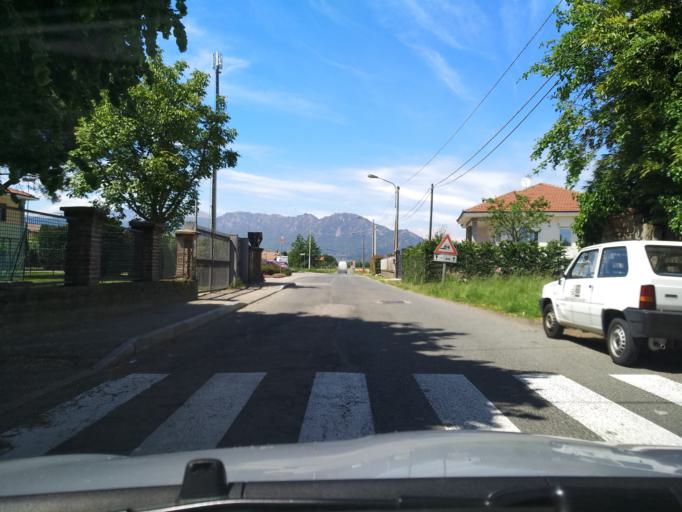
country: IT
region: Piedmont
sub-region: Provincia di Torino
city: Riva
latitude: 44.8936
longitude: 7.3844
